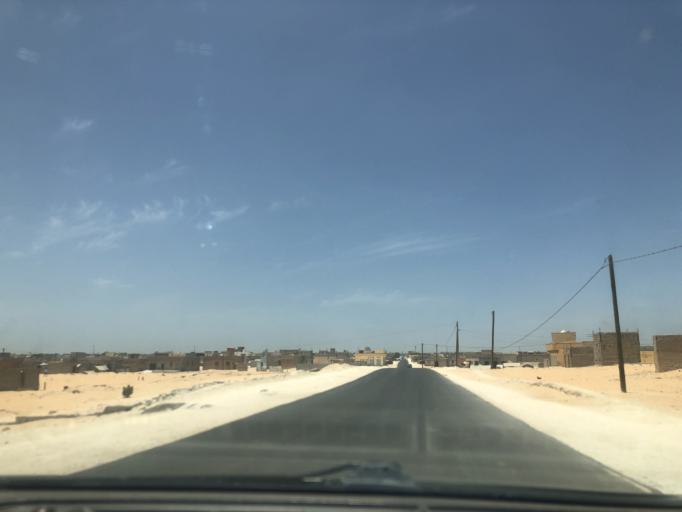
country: MR
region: Nouakchott
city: Nouakchott
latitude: 18.0038
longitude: -15.9600
